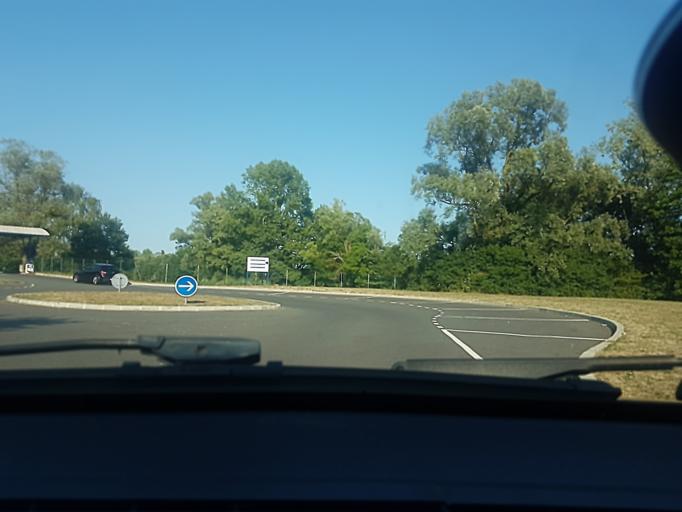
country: FR
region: Bourgogne
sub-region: Departement de Saone-et-Loire
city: Sennecey-le-Grand
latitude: 46.6676
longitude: 4.8214
